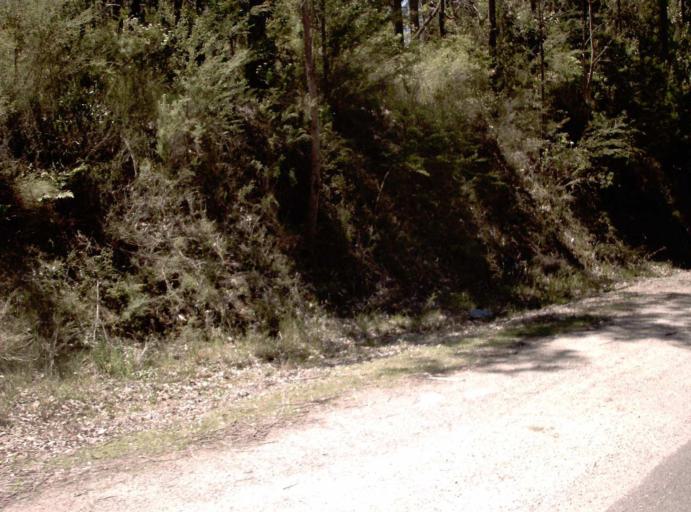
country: AU
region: Victoria
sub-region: East Gippsland
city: Lakes Entrance
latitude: -37.7034
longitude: 148.7127
